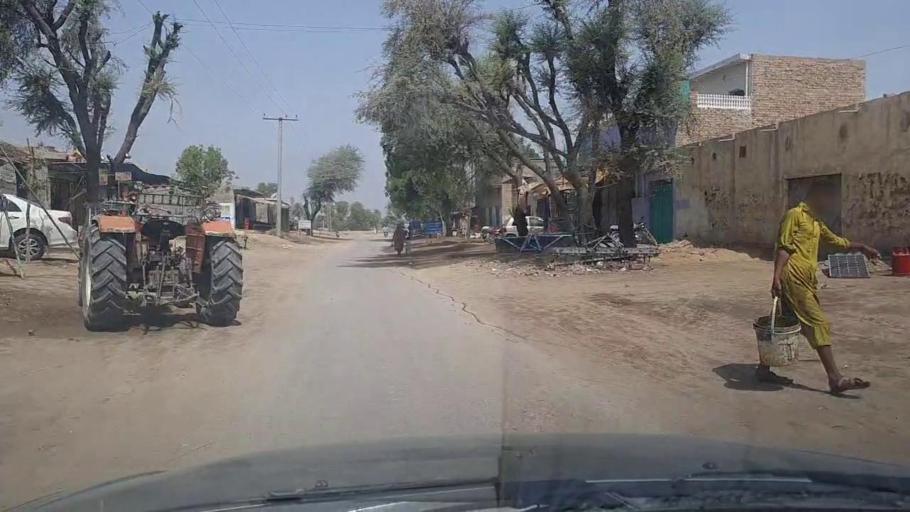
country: PK
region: Sindh
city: Setharja Old
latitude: 27.1326
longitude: 68.5319
